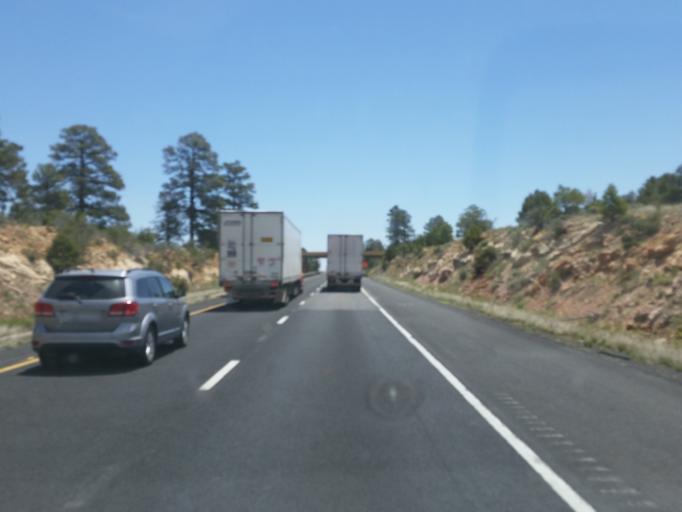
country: US
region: Arizona
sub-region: Coconino County
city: Flagstaff
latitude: 35.2089
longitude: -111.5195
